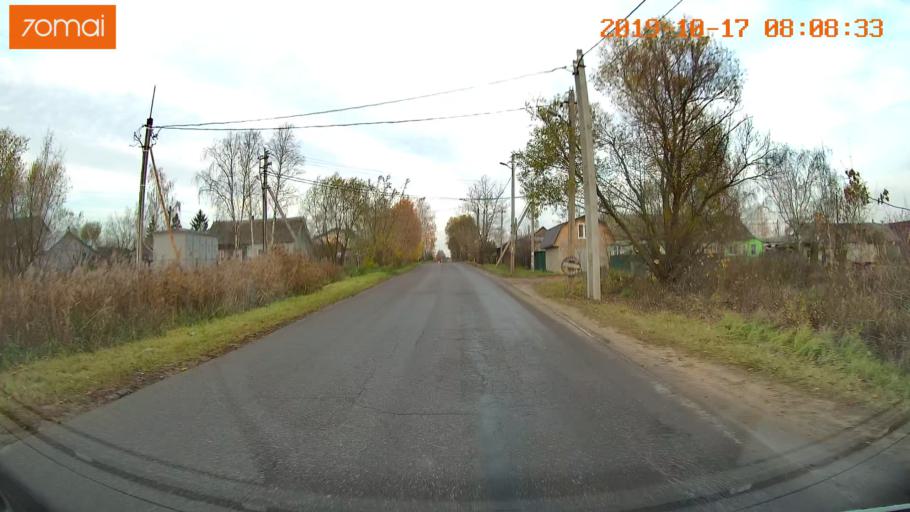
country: RU
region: Vladimir
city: Kol'chugino
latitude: 56.3145
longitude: 39.3869
